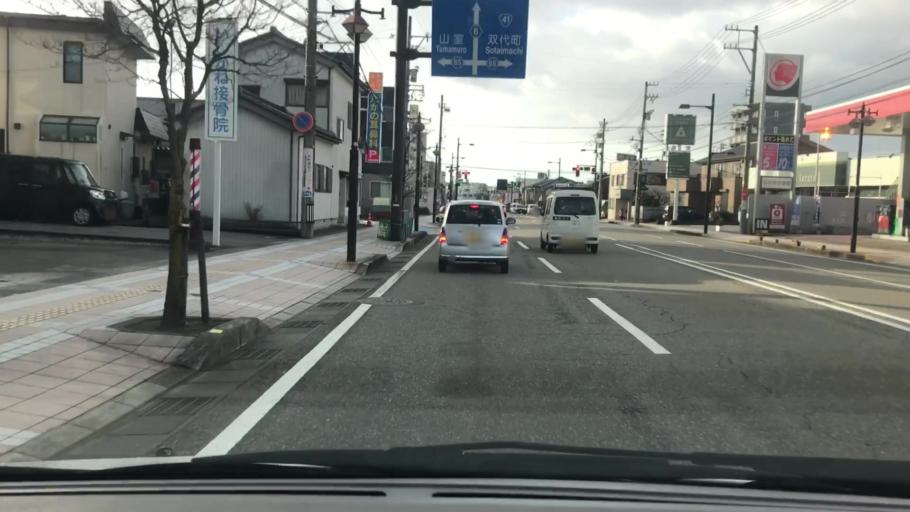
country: JP
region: Toyama
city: Toyama-shi
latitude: 36.6874
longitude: 137.2377
